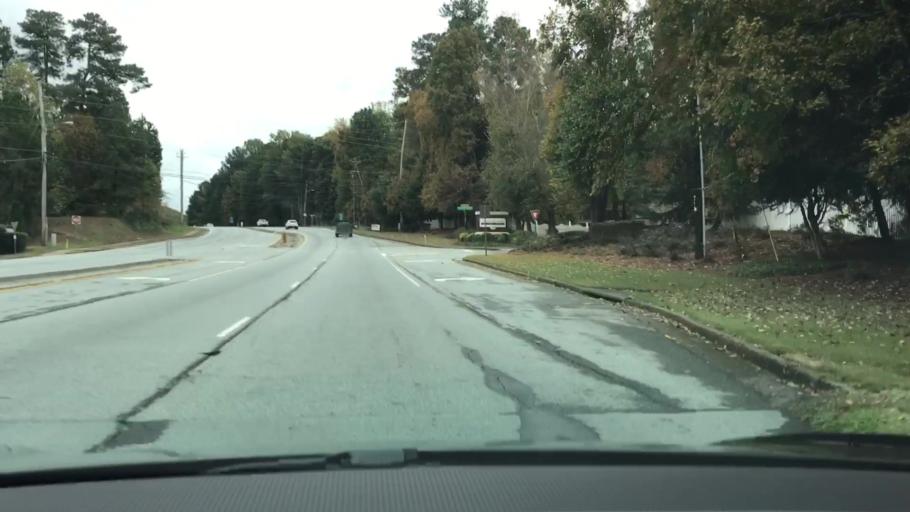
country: US
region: Georgia
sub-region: Gwinnett County
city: Lawrenceville
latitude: 33.9776
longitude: -84.0201
